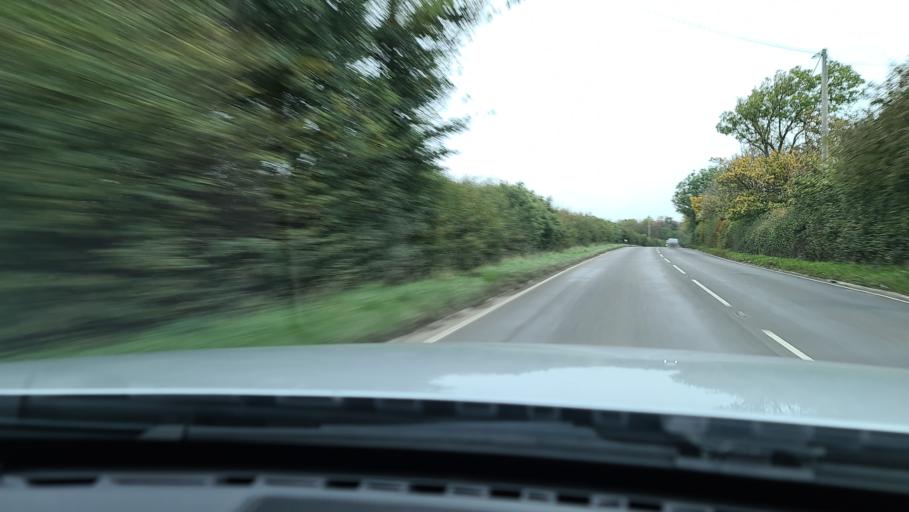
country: GB
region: England
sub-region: Buckinghamshire
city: Waddesdon
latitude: 51.8589
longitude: -0.9854
